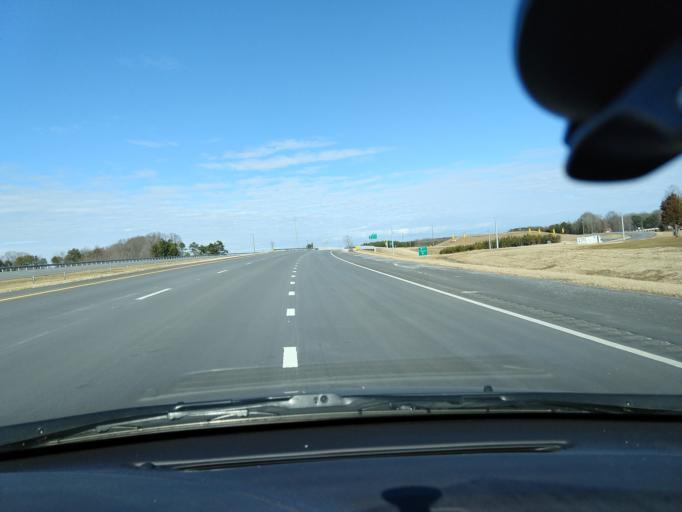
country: US
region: North Carolina
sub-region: Guilford County
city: Oak Ridge
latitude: 36.1314
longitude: -79.9658
